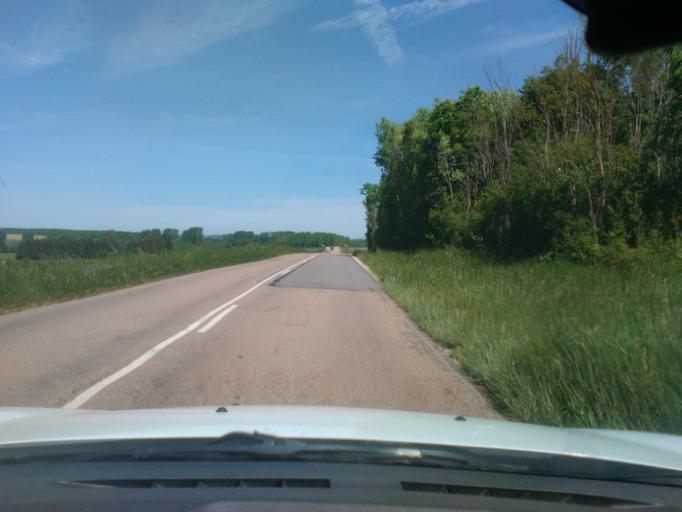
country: FR
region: Lorraine
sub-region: Departement des Vosges
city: Rambervillers
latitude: 48.3971
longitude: 6.5914
